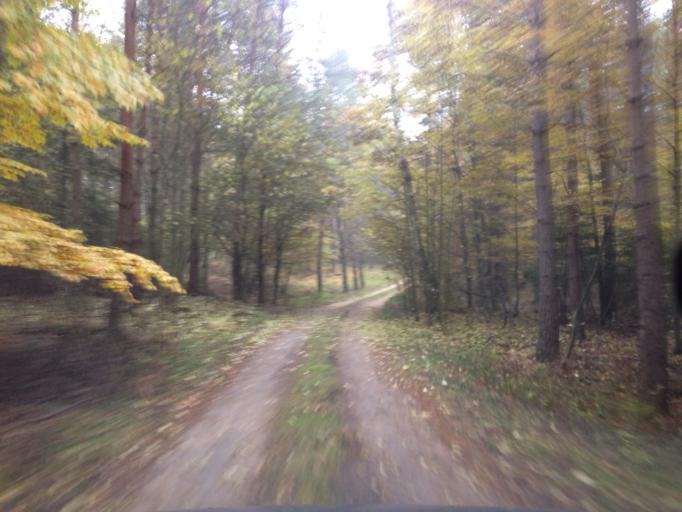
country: PL
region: Kujawsko-Pomorskie
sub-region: Powiat brodnicki
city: Gorzno
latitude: 53.2220
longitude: 19.7170
